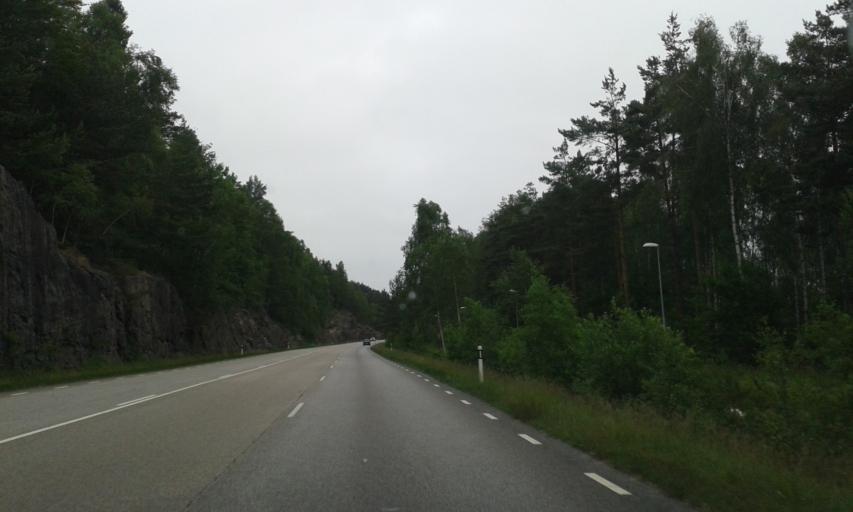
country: SE
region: Vaestra Goetaland
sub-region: Partille Kommun
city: Partille
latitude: 57.7445
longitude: 12.0783
